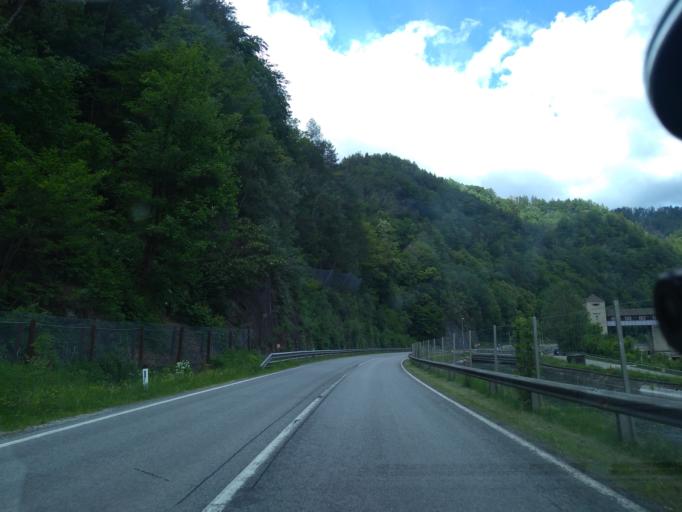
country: AT
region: Styria
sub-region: Politischer Bezirk Bruck-Muerzzuschlag
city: Pernegg an der Mur
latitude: 47.3726
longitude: 15.3088
